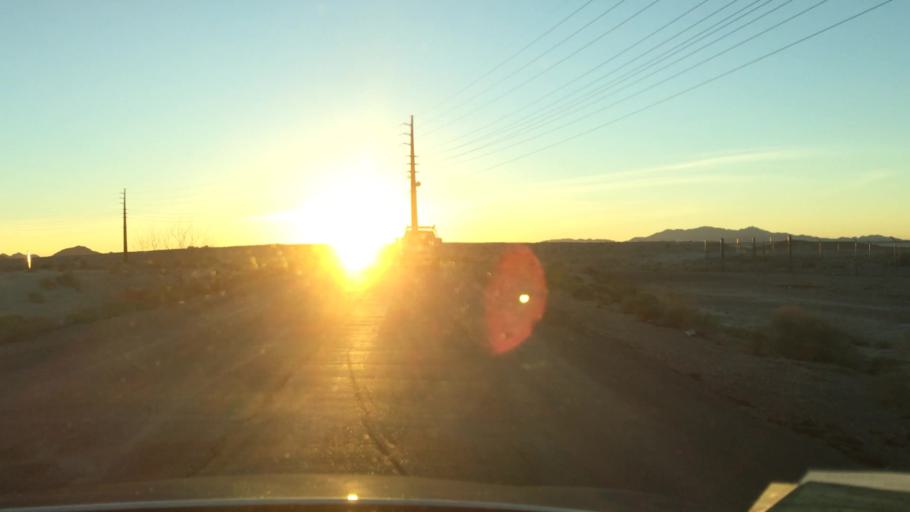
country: US
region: Nevada
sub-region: Clark County
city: Nellis Air Force Base
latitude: 36.2216
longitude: -114.8897
